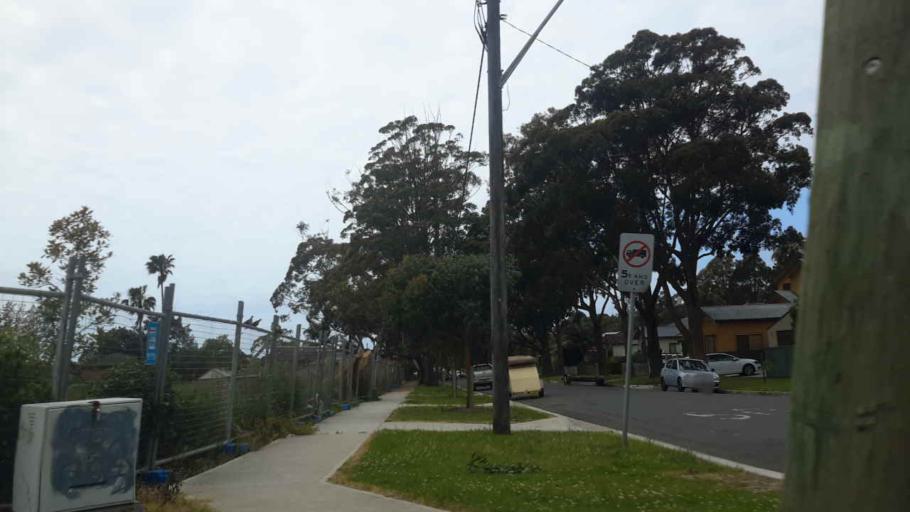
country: AU
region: New South Wales
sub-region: Wollongong
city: Corrimal
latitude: -34.3602
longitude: 150.8996
